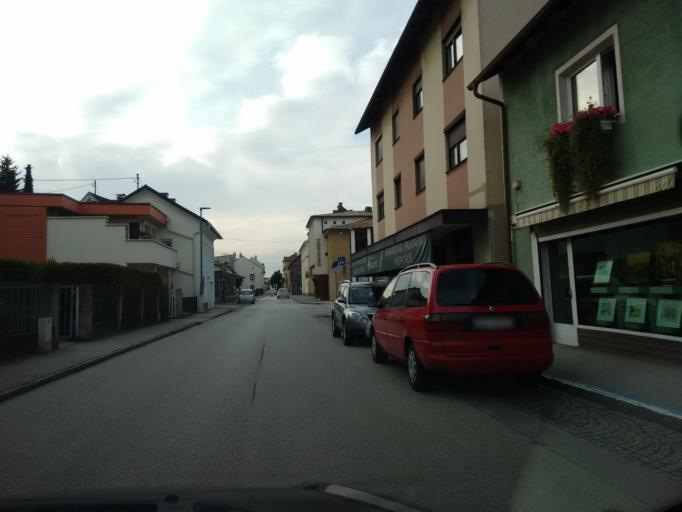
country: AT
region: Upper Austria
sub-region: Politischer Bezirk Steyr-Land
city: Bad Hall
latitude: 48.0327
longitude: 14.2132
